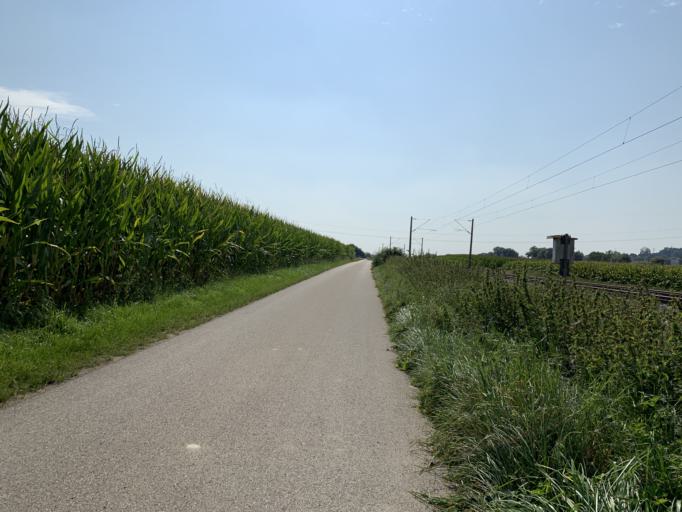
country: DE
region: Bavaria
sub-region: Upper Bavaria
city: Langenbach
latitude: 48.4219
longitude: 11.8239
